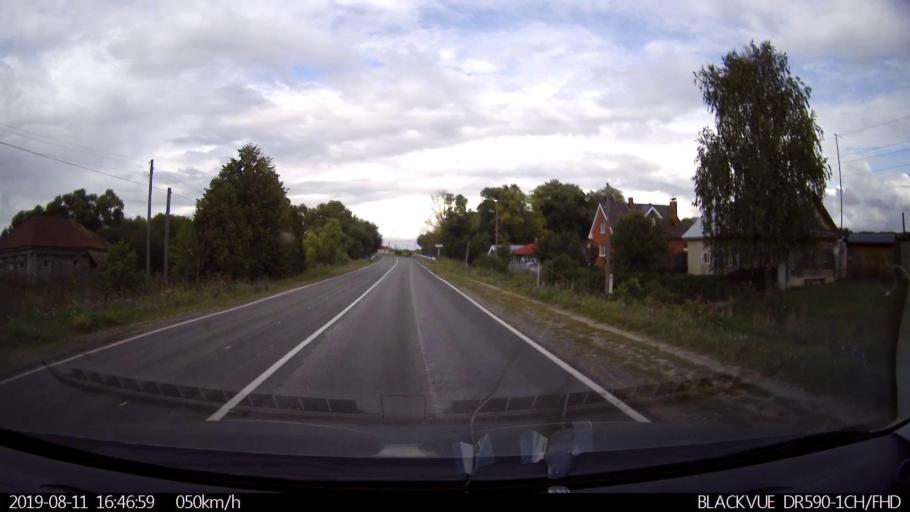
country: RU
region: Ulyanovsk
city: Mayna
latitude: 54.2007
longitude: 47.6934
